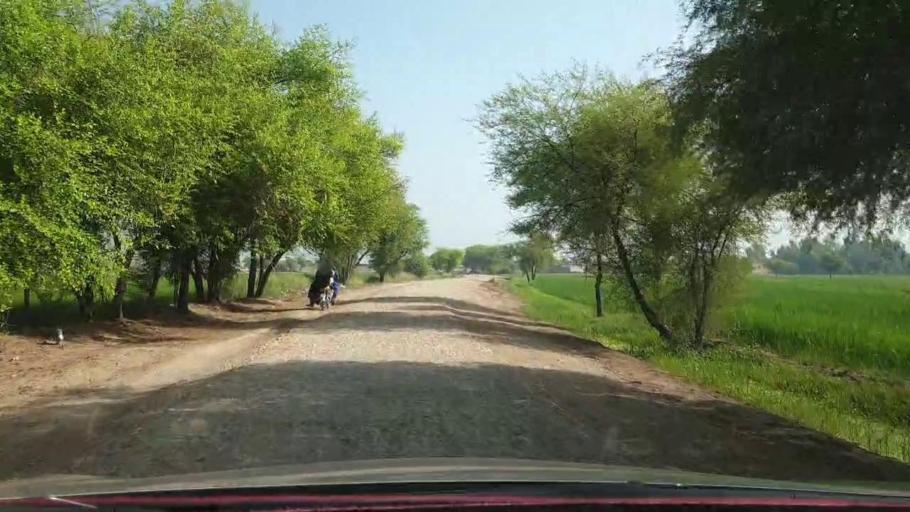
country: PK
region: Sindh
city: Nasirabad
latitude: 27.4585
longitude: 67.9180
